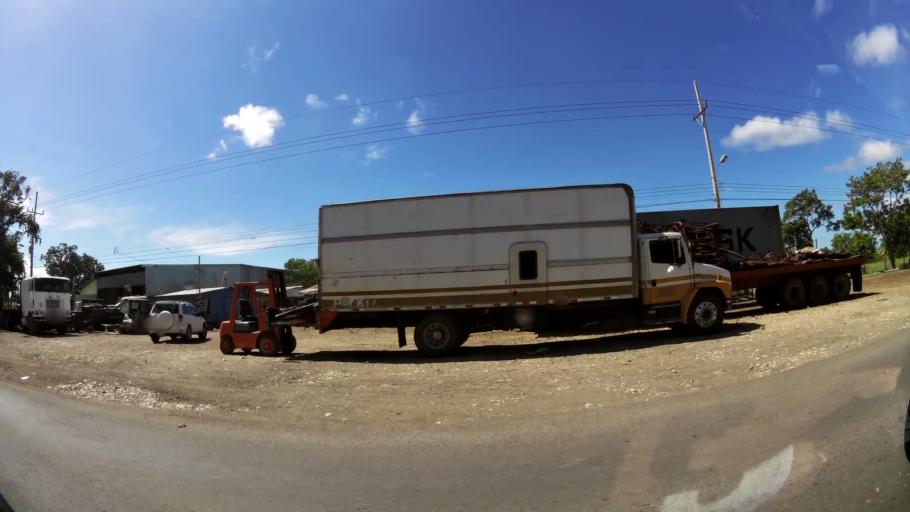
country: CR
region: Guanacaste
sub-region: Canton de Canas
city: Canas
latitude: 10.4134
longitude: -85.0860
